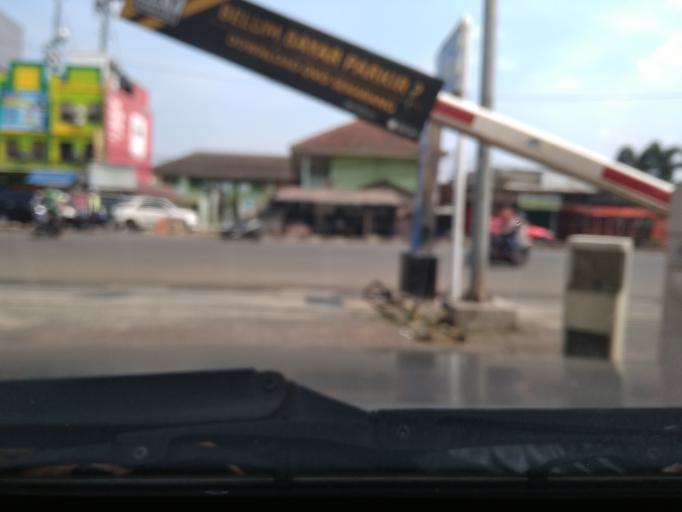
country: ID
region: West Java
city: Ciputat
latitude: -6.2651
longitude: 106.6549
